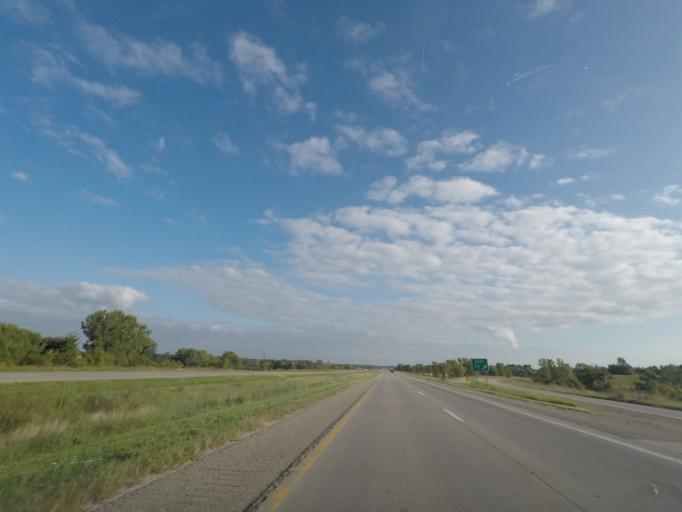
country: US
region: Iowa
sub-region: Polk County
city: Pleasant Hill
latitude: 41.5937
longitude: -93.4987
